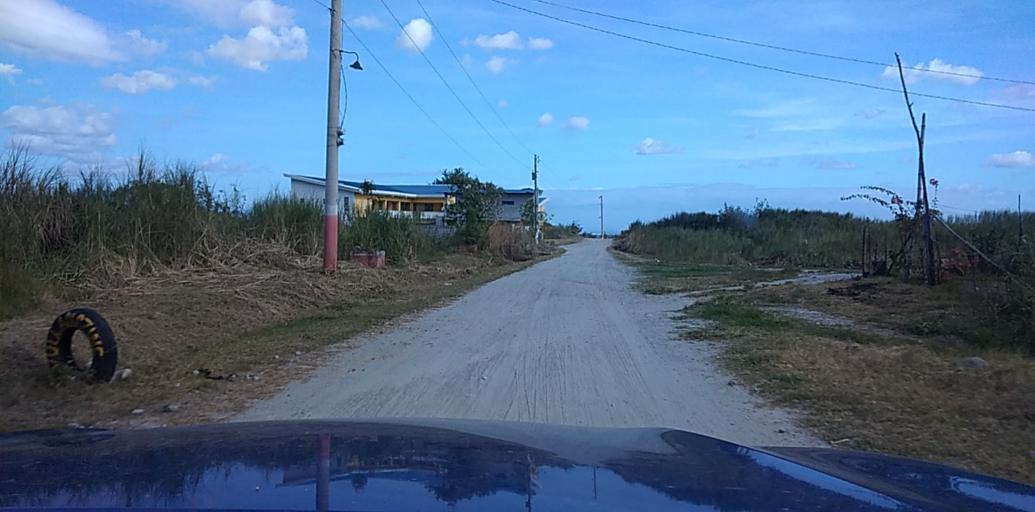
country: PH
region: Central Luzon
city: Santol
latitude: 15.1431
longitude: 120.5262
